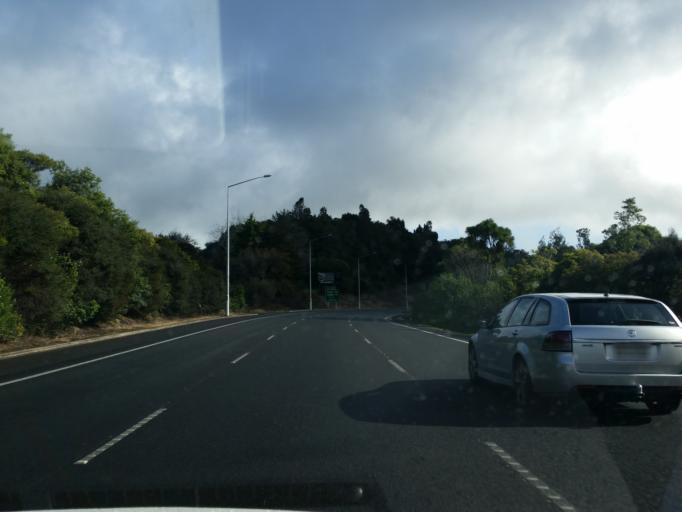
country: NZ
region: Auckland
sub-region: Auckland
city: Pukekohe East
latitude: -37.2213
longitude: 175.0029
